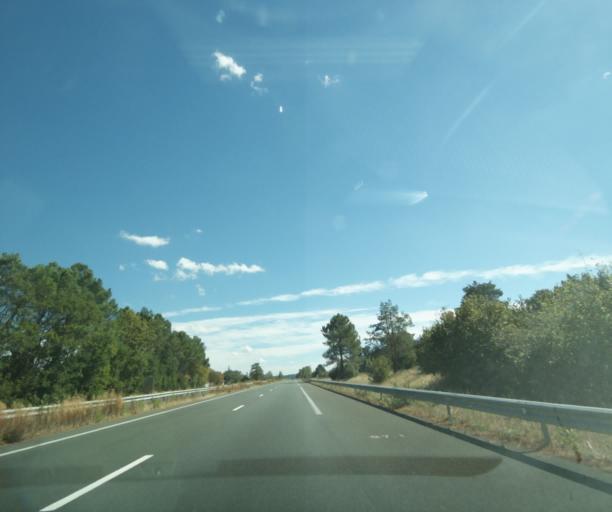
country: FR
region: Aquitaine
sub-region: Departement du Lot-et-Garonne
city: Buzet-sur-Baise
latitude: 44.2503
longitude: 0.3004
